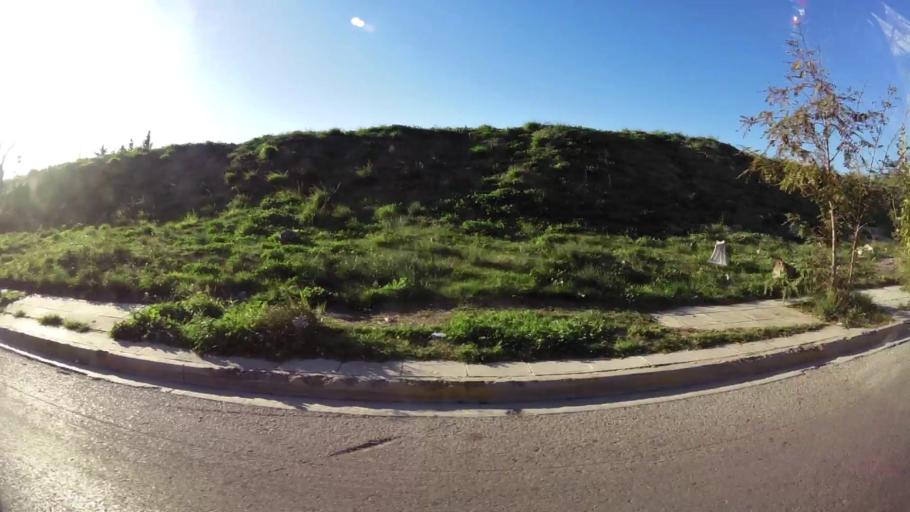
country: GR
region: Attica
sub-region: Nomarchia Anatolikis Attikis
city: Acharnes
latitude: 38.0821
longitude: 23.7256
